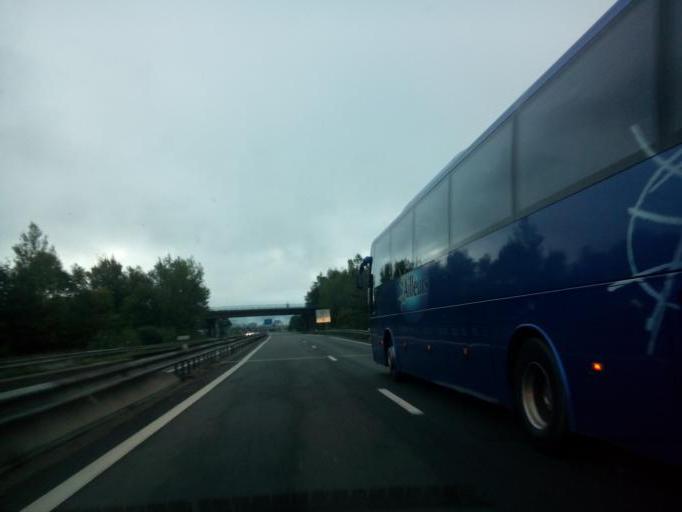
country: FR
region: Rhone-Alpes
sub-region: Departement de l'Isere
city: Romagnieu
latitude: 45.5731
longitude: 5.6513
